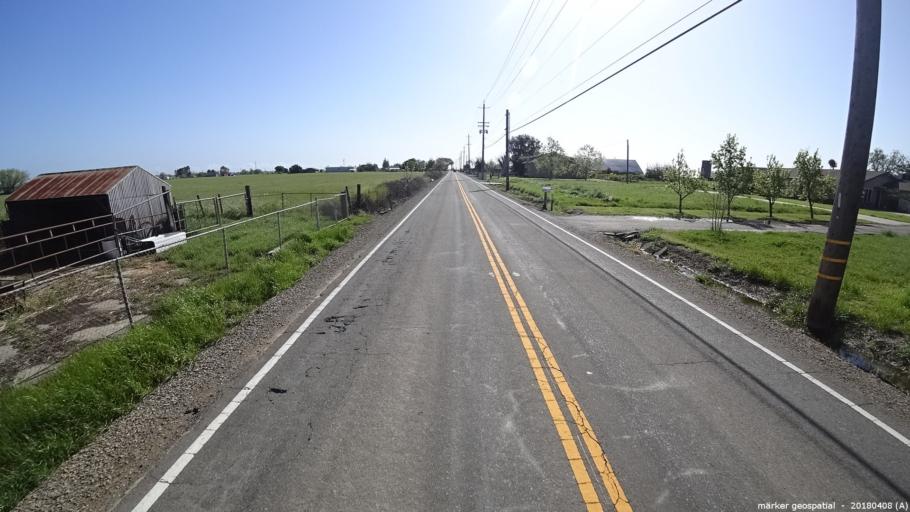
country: US
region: California
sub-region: Sacramento County
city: Elk Grove
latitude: 38.3724
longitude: -121.4061
